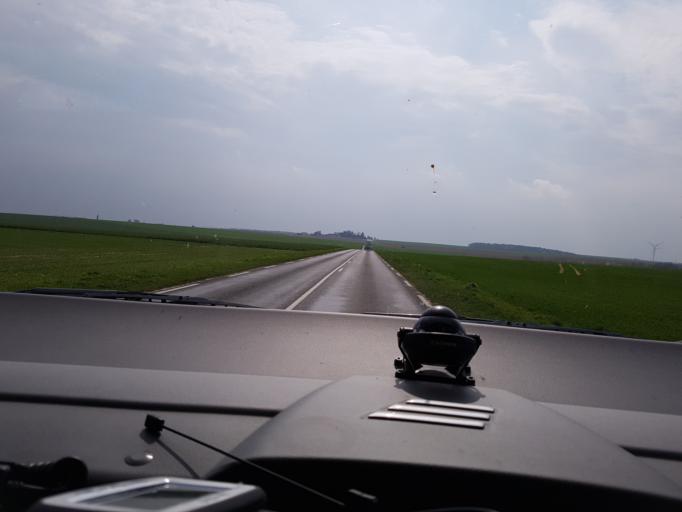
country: FR
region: Picardie
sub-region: Departement de l'Aisne
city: Crouy
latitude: 49.4598
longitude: 3.3515
